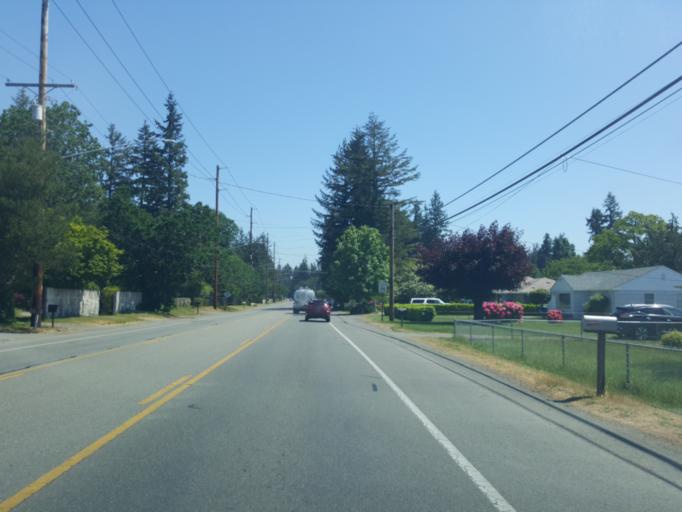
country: US
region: Washington
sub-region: Pierce County
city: Lakewood
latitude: 47.1485
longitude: -122.5508
